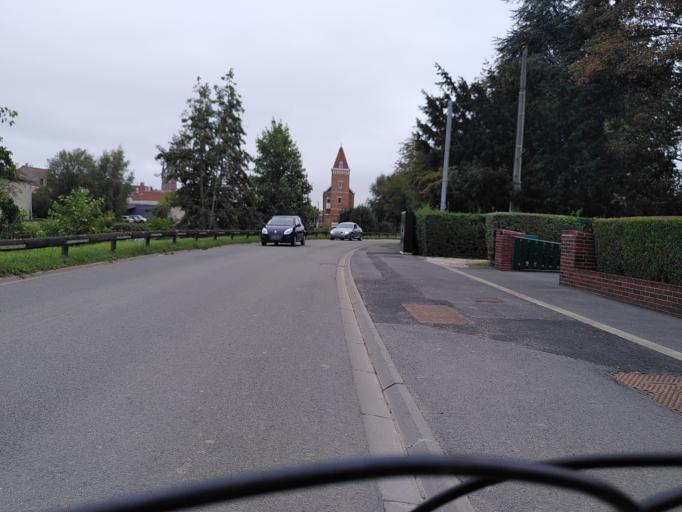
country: FR
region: Nord-Pas-de-Calais
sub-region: Departement du Nord
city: Merville
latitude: 50.6391
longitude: 2.6365
